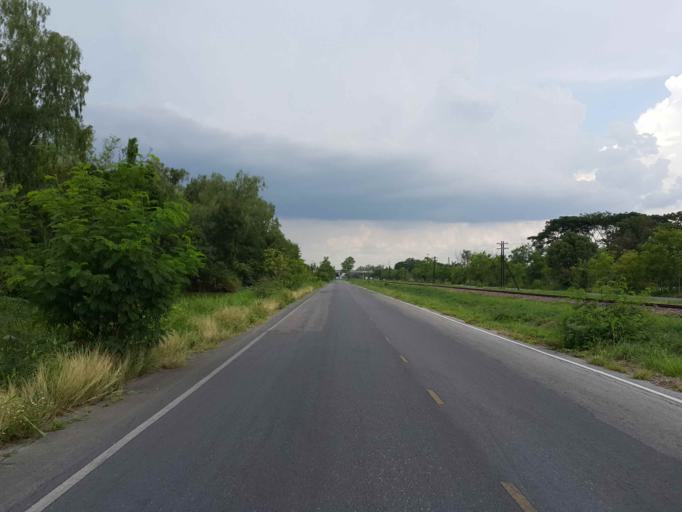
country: TH
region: Chiang Mai
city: Saraphi
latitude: 18.7399
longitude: 99.0291
